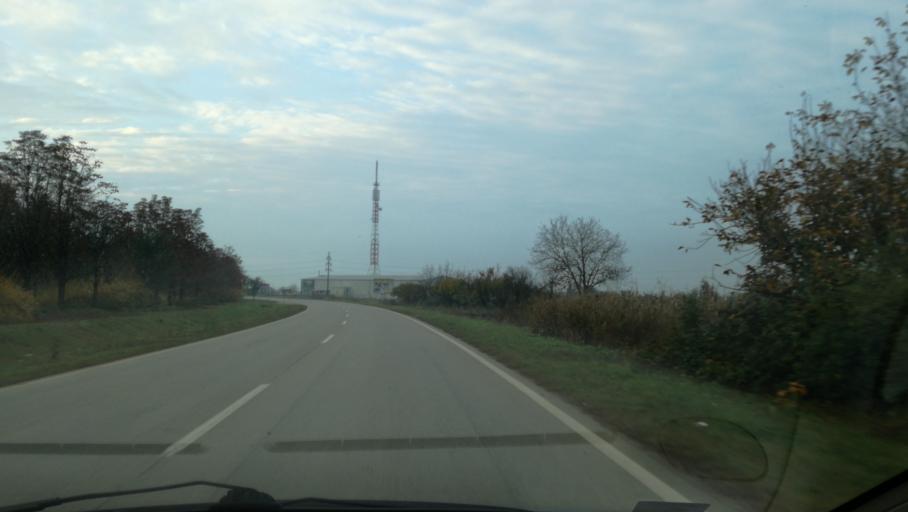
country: RS
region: Autonomna Pokrajina Vojvodina
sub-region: Severnobanatski Okrug
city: Kikinda
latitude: 45.8114
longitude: 20.4325
